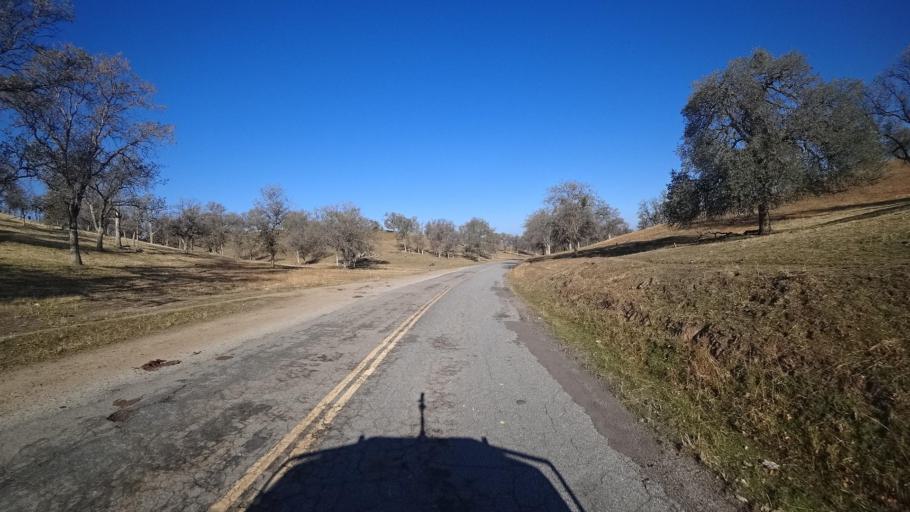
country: US
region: California
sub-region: Kern County
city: Alta Sierra
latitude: 35.7371
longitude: -118.8187
